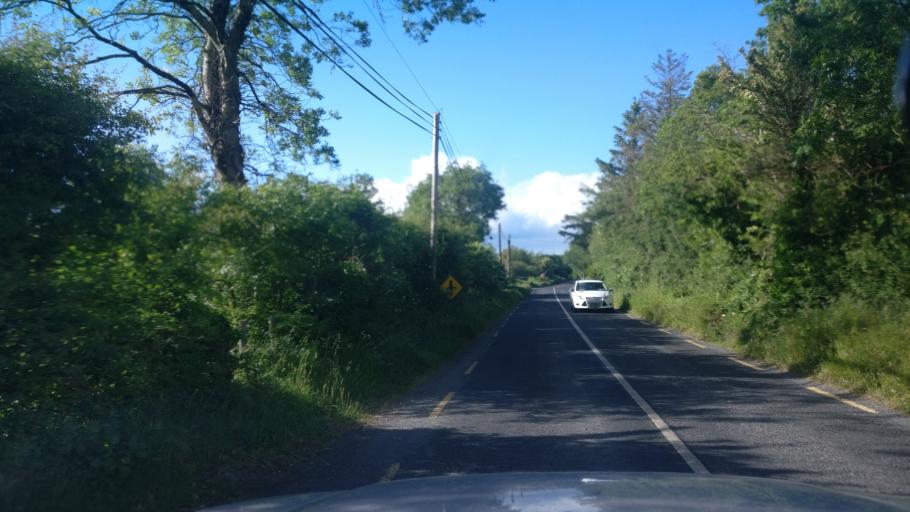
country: IE
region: Connaught
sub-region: County Galway
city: Portumna
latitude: 53.1948
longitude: -8.3033
